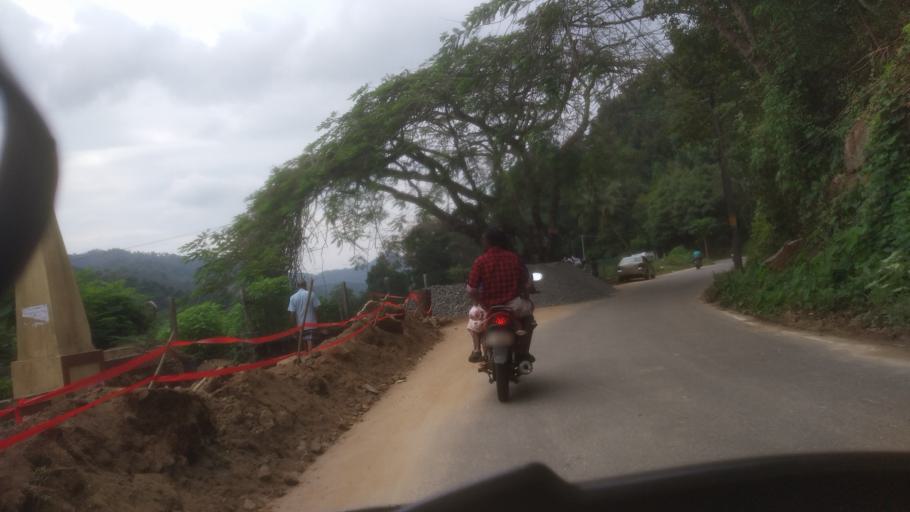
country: IN
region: Kerala
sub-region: Idukki
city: Munnar
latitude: 9.9805
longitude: 77.0008
